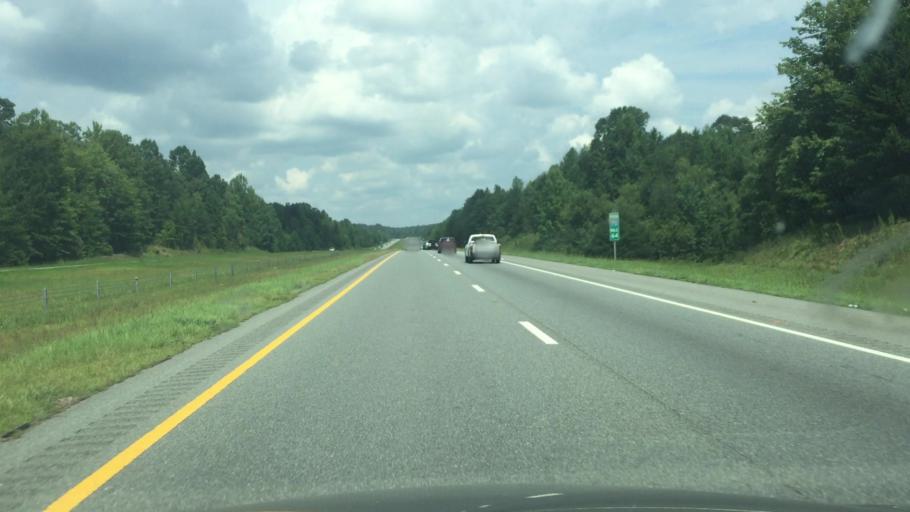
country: US
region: North Carolina
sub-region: Randolph County
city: Asheboro
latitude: 35.5666
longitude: -79.8047
